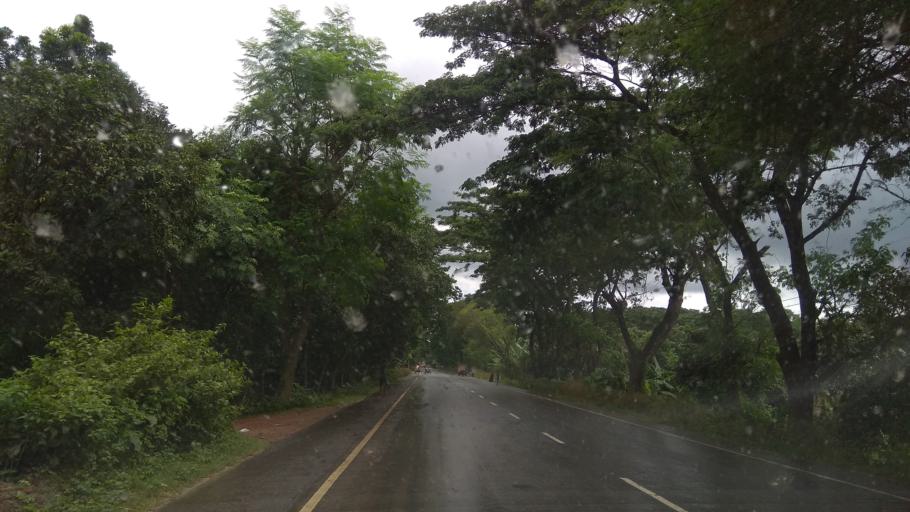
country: BD
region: Khulna
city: Kalia
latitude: 23.2485
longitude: 89.7572
